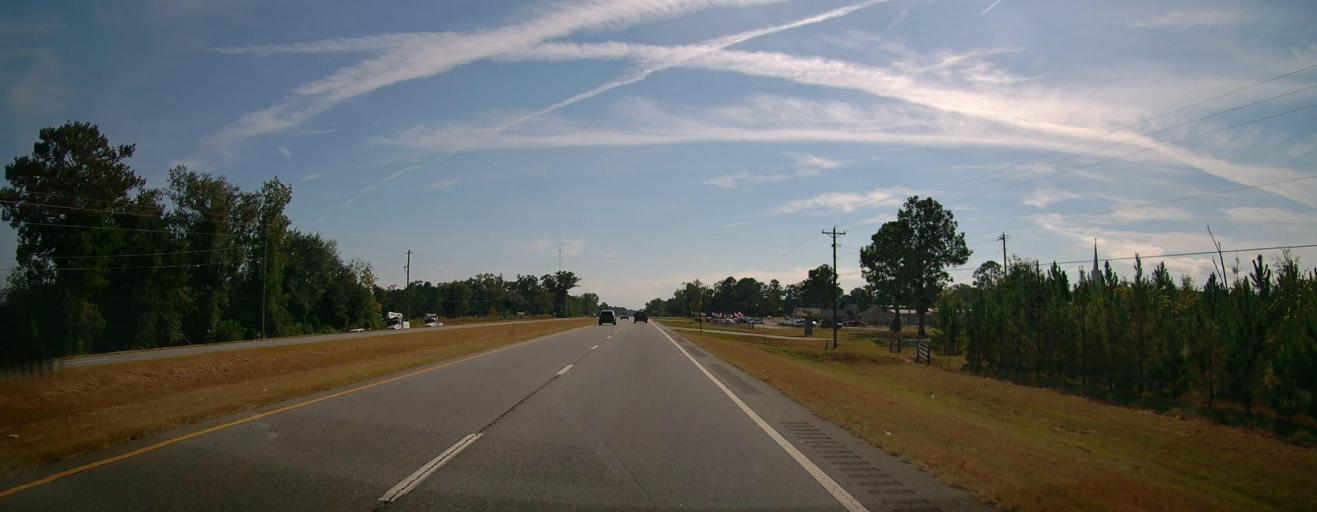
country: US
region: Georgia
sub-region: Dougherty County
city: Putney
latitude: 31.5118
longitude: -84.1156
